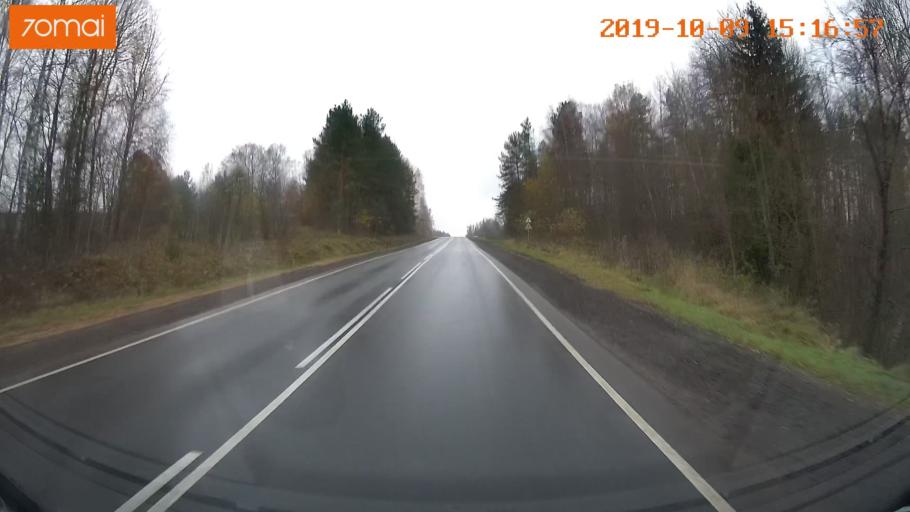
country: RU
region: Kostroma
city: Susanino
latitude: 58.1048
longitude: 41.5845
